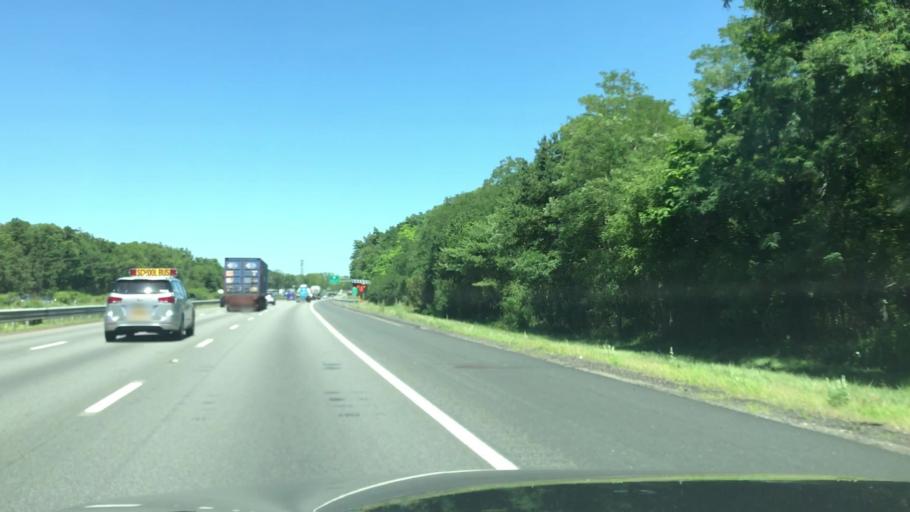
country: US
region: Massachusetts
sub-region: Norfolk County
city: Plainville
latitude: 41.9959
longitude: -71.2917
